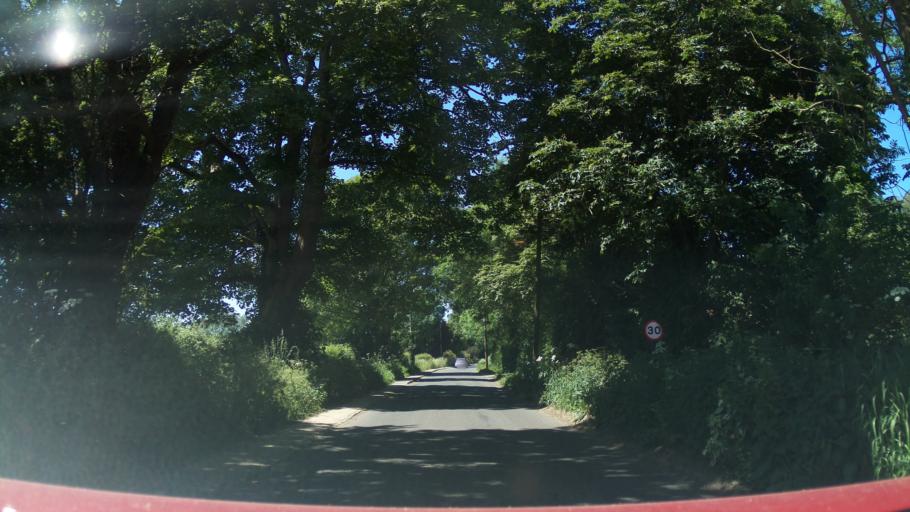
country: GB
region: England
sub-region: Wiltshire
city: Bremhill
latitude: 51.4732
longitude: -2.0552
